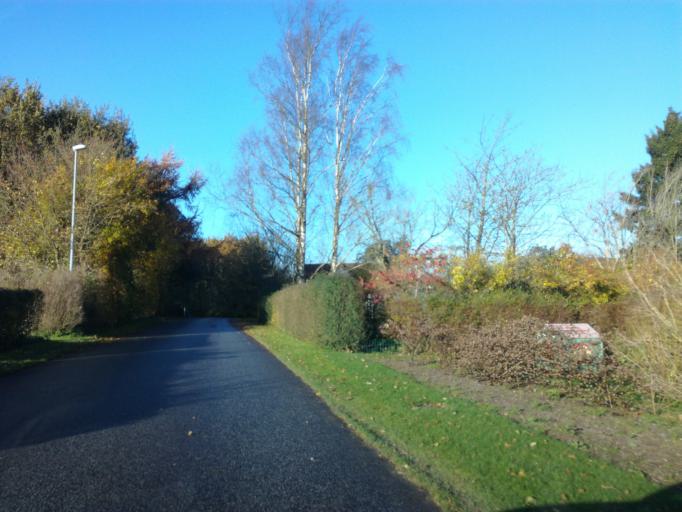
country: DK
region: South Denmark
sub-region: Vejle Kommune
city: Borkop
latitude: 55.6021
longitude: 9.6634
